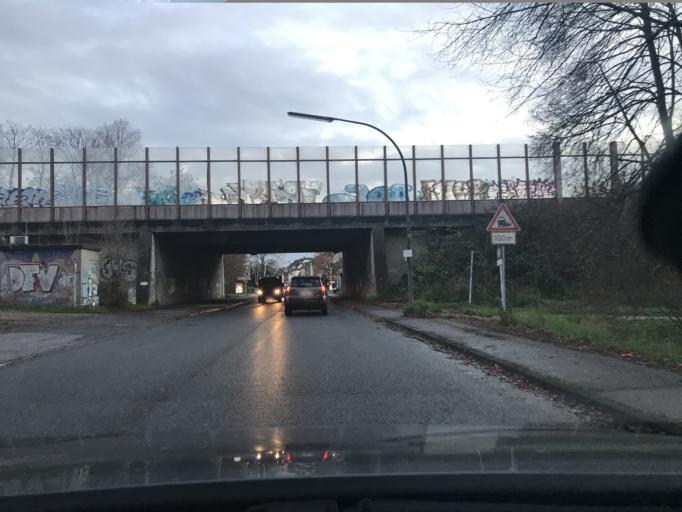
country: DE
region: North Rhine-Westphalia
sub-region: Regierungsbezirk Koln
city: Rath
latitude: 50.9504
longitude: 7.0788
